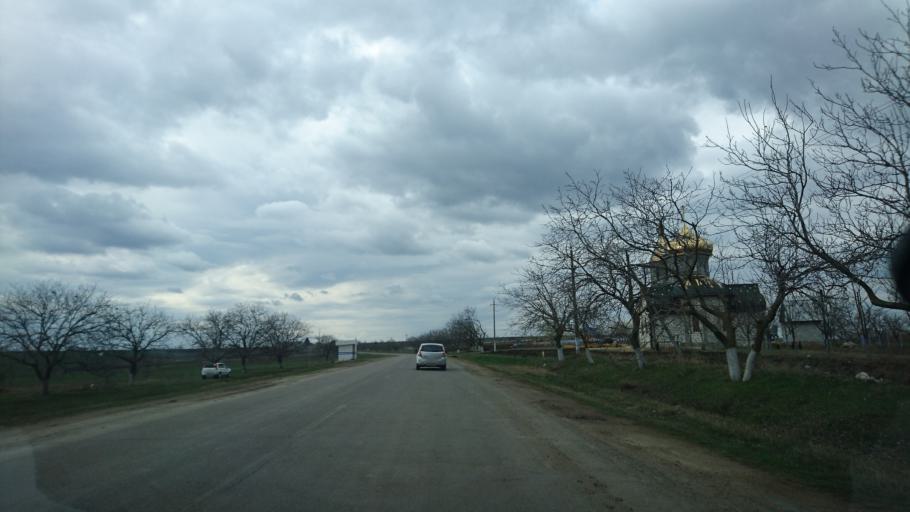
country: MD
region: Gagauzia
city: Comrat
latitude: 46.3061
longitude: 28.6228
